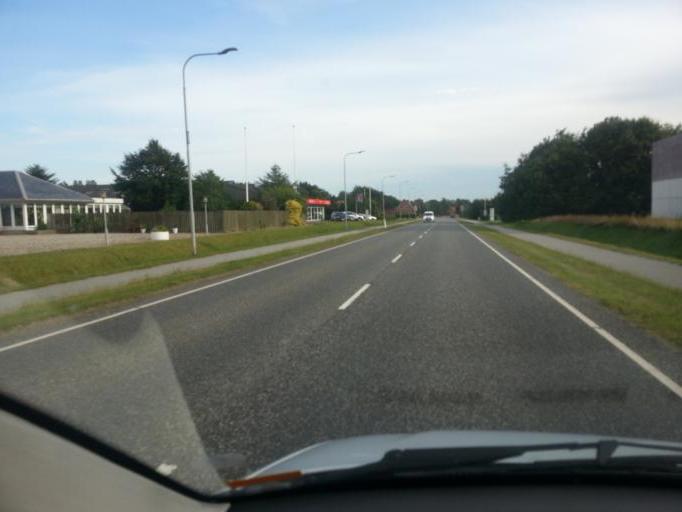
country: DK
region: South Denmark
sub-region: Vejen Kommune
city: Holsted
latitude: 55.4921
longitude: 8.9149
